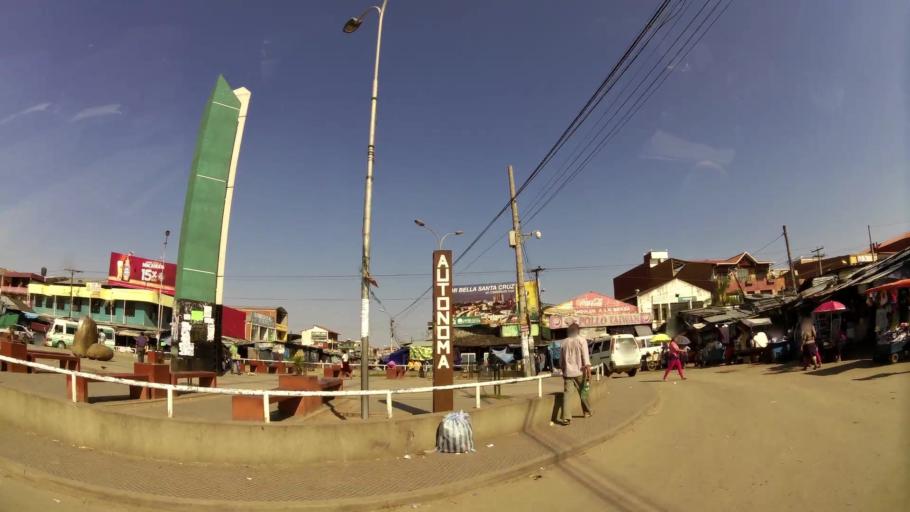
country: BO
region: Santa Cruz
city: Santa Cruz de la Sierra
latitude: -17.8250
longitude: -63.1319
